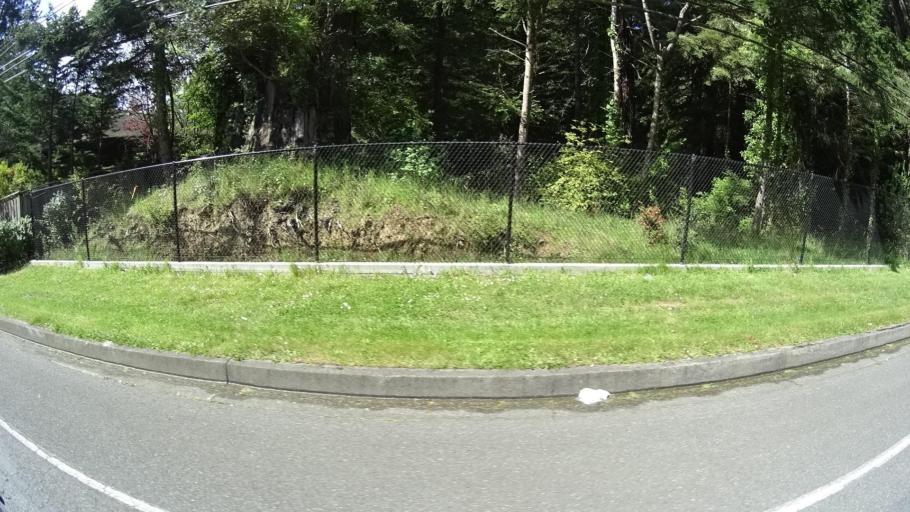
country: US
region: California
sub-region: Humboldt County
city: Cutten
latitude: 40.7689
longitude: -124.1592
